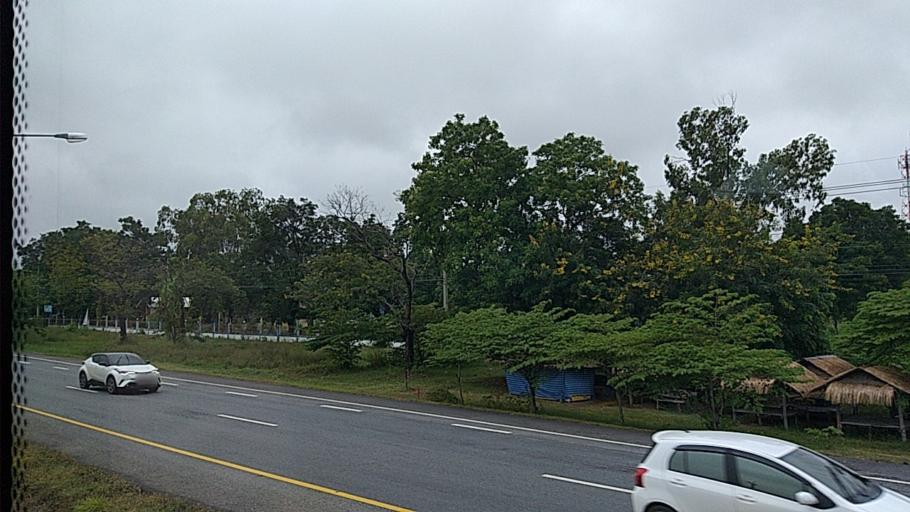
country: TH
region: Nakhon Ratchasima
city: Non Daeng
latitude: 15.3794
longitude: 102.4620
